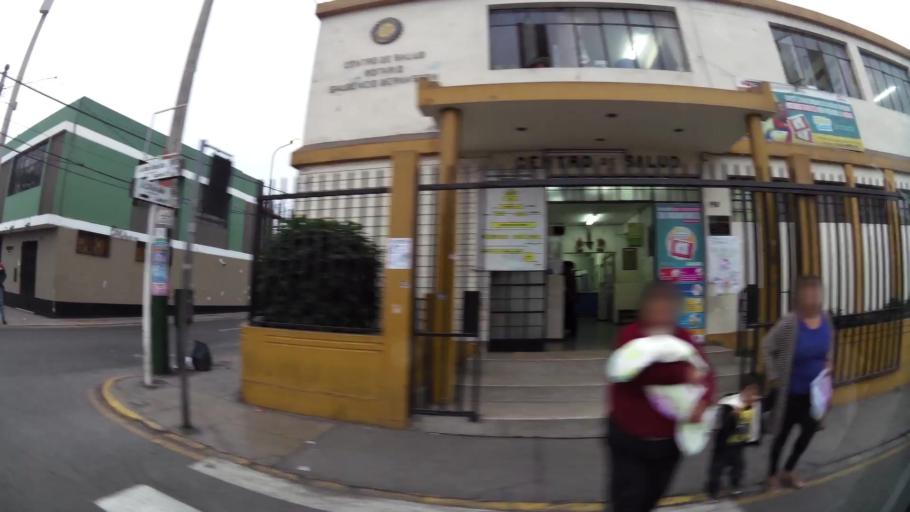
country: PE
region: Lima
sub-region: Lima
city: Surco
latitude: -12.1505
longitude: -77.0204
